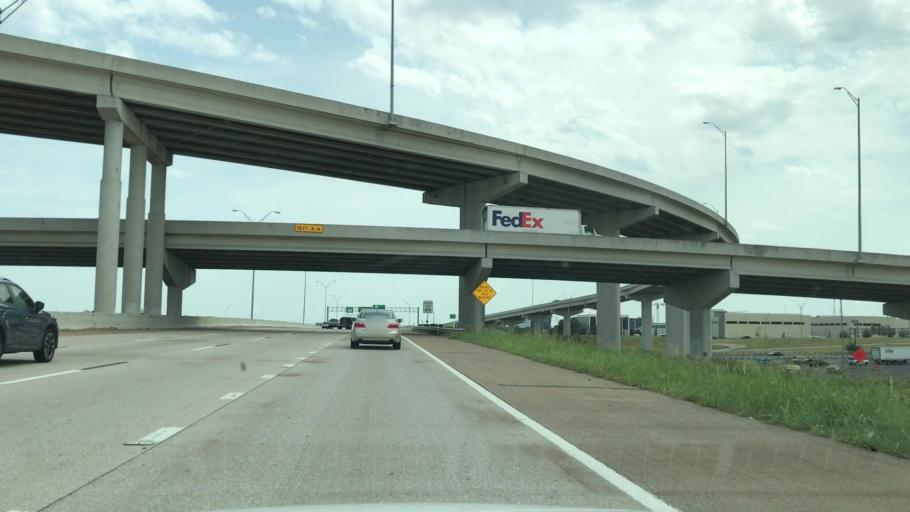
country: US
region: Texas
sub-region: Tarrant County
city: Euless
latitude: 32.8397
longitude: -97.0613
